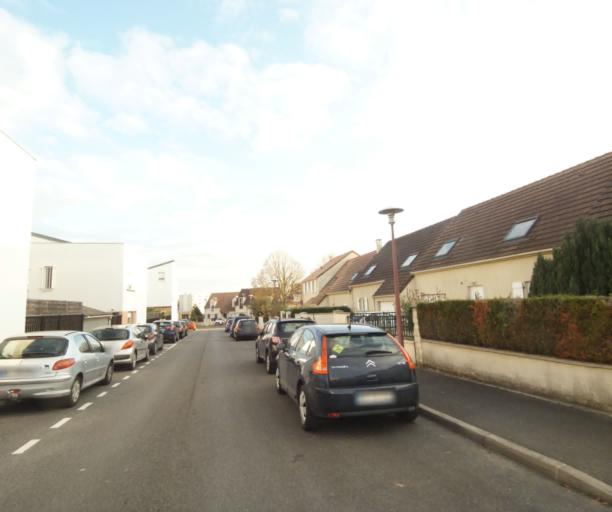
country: FR
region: Ile-de-France
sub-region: Departement du Val-d'Oise
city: Arnouville
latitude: 48.9891
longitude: 2.4270
